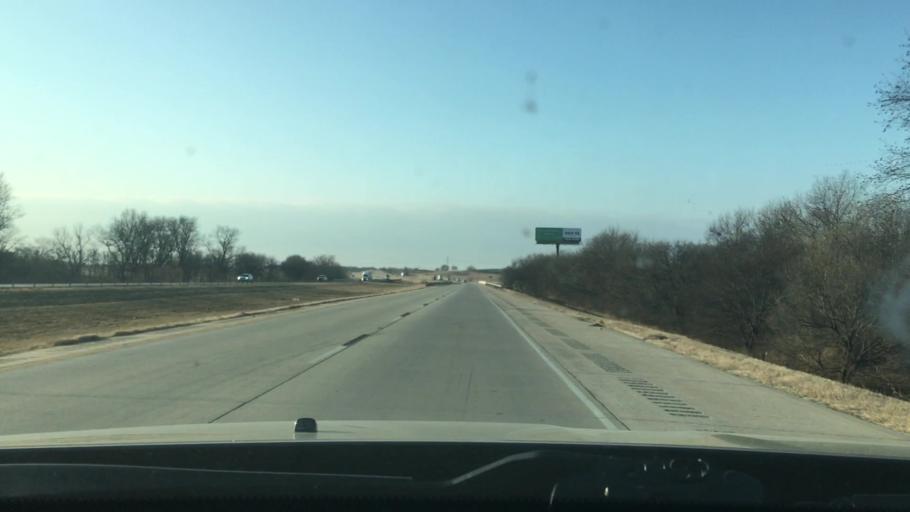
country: US
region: Oklahoma
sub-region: Carter County
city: Ardmore
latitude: 34.2670
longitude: -97.1638
